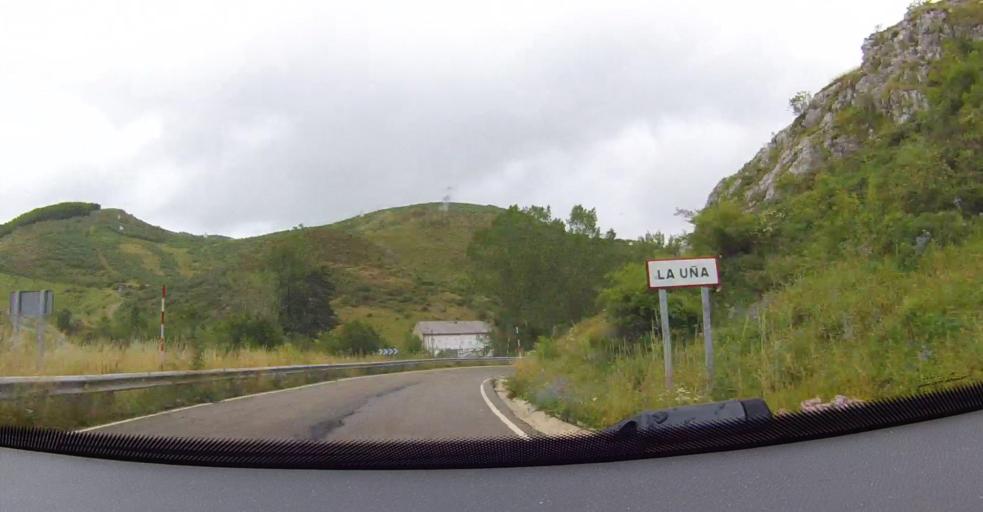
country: ES
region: Castille and Leon
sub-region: Provincia de Leon
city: Acebedo
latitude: 43.0661
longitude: -5.1377
